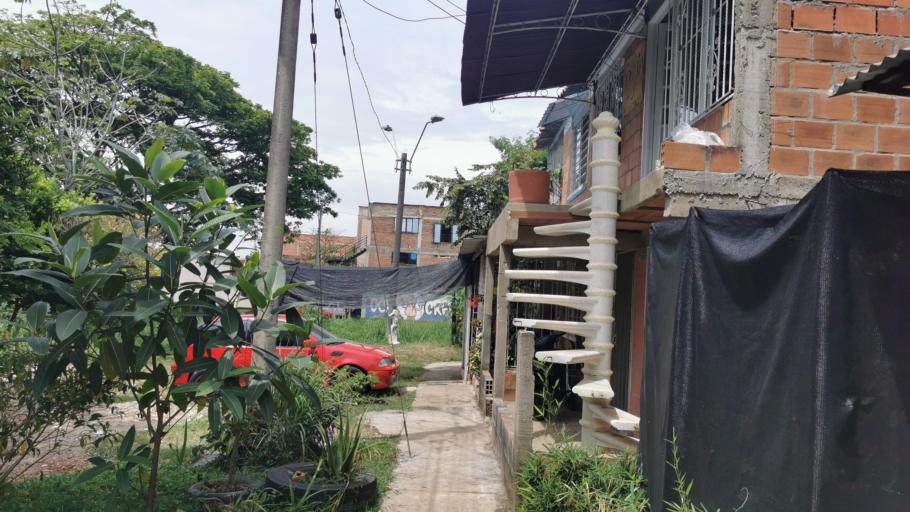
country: CO
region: Valle del Cauca
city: Jamundi
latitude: 3.2526
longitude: -76.5363
